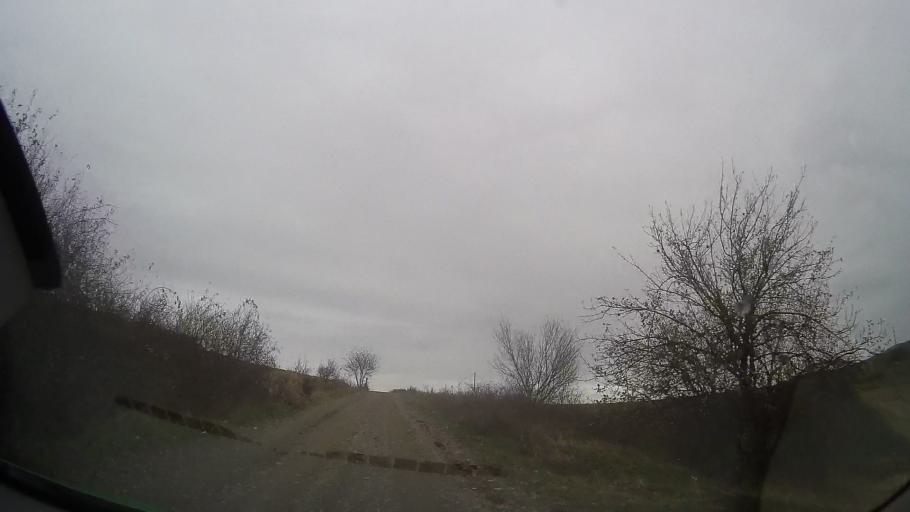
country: RO
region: Mures
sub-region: Comuna Bala
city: Bala
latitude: 46.6991
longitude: 24.4919
